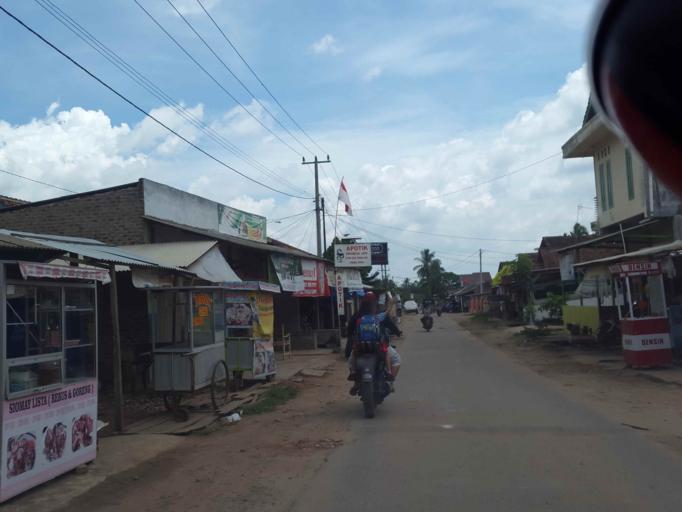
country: ID
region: Lampung
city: Natar
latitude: -5.3160
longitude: 105.2023
